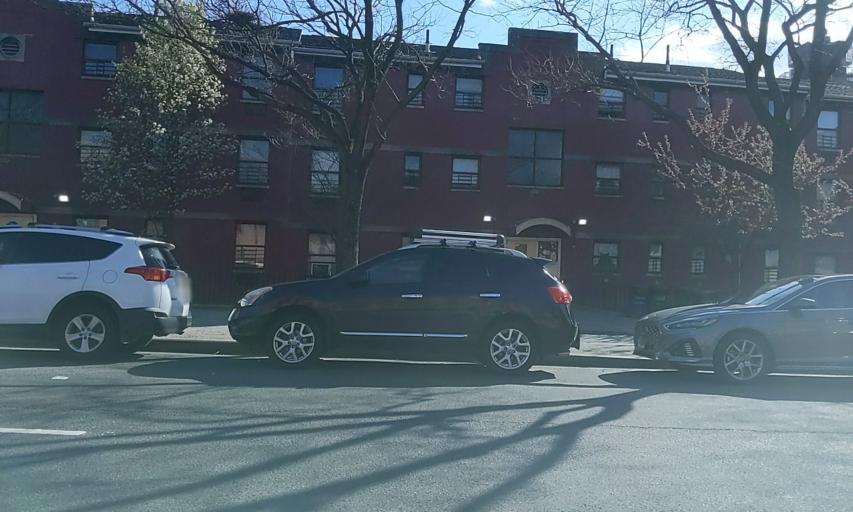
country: US
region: New York
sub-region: Bronx
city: The Bronx
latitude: 40.8378
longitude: -73.9004
